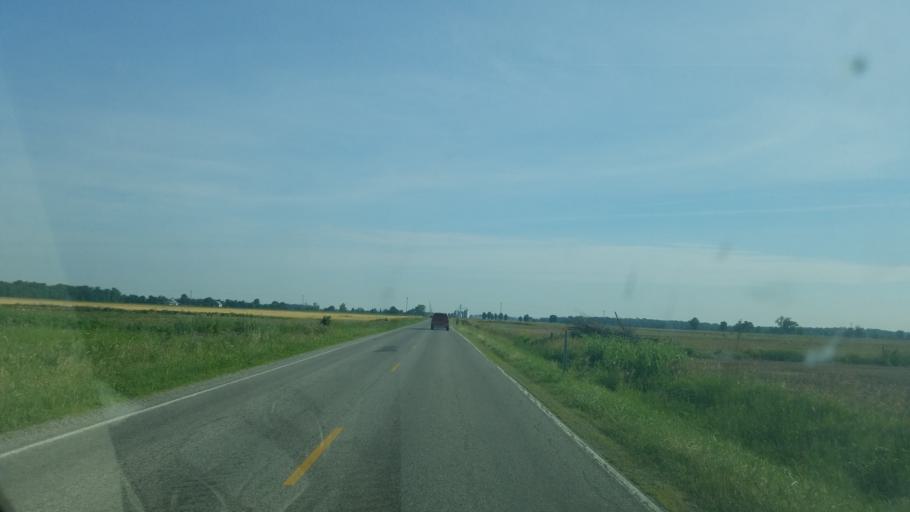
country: US
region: Ohio
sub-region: Hancock County
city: Arlington
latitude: 40.9612
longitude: -83.6985
